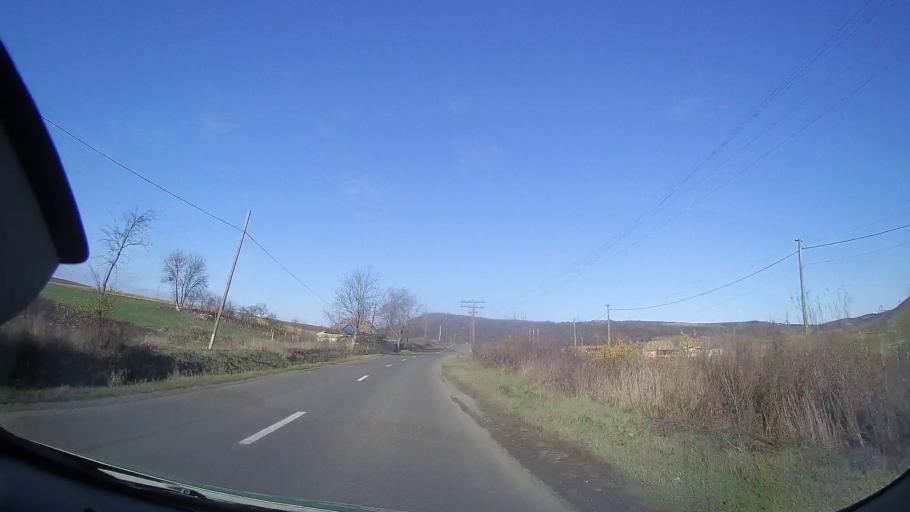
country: RO
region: Mures
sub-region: Comuna Mihesu de Campie
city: Mihesu de Campie
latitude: 46.6631
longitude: 24.1744
